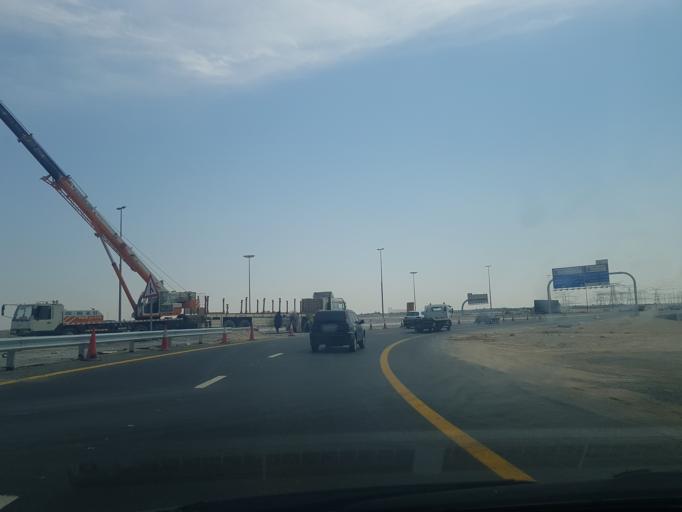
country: AE
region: Ash Shariqah
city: Sharjah
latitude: 25.2401
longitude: 55.5664
